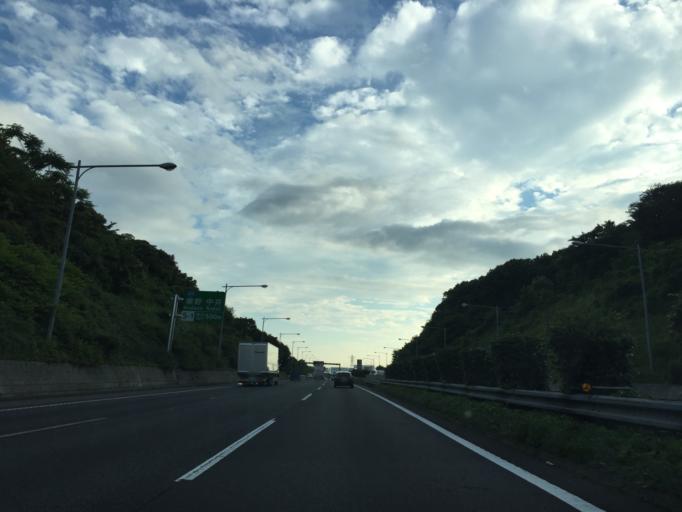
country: JP
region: Kanagawa
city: Hadano
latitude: 35.3563
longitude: 139.2420
